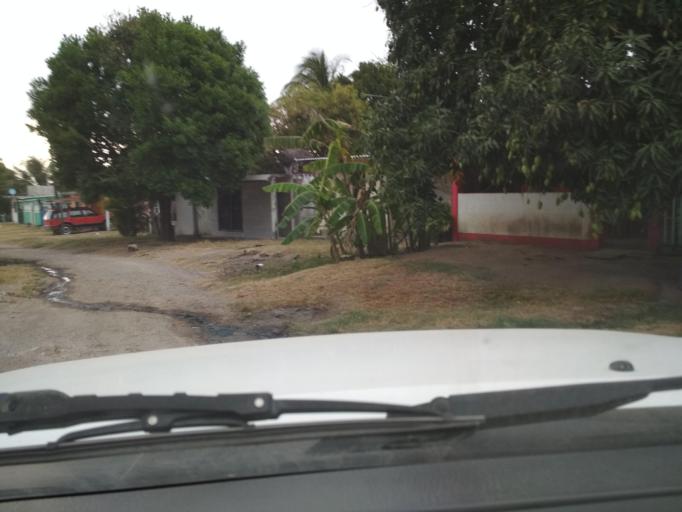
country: MX
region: Veracruz
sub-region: Medellin
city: Fraccionamiento Arboledas San Ramon
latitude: 19.0837
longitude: -96.1530
